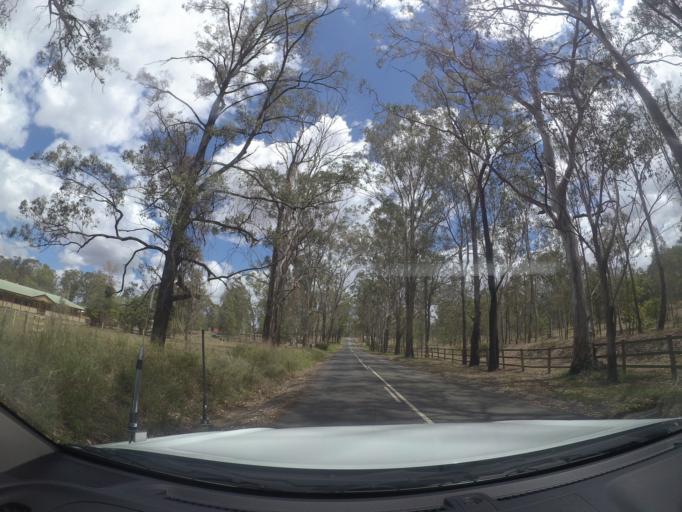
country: AU
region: Queensland
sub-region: Logan
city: Cedar Vale
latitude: -27.9373
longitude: 153.0694
